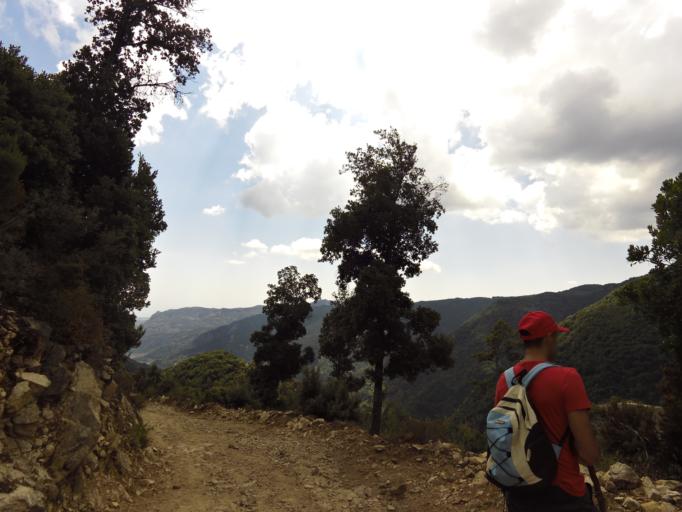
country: IT
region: Calabria
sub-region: Provincia di Reggio Calabria
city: Bivongi
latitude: 38.5071
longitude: 16.3966
